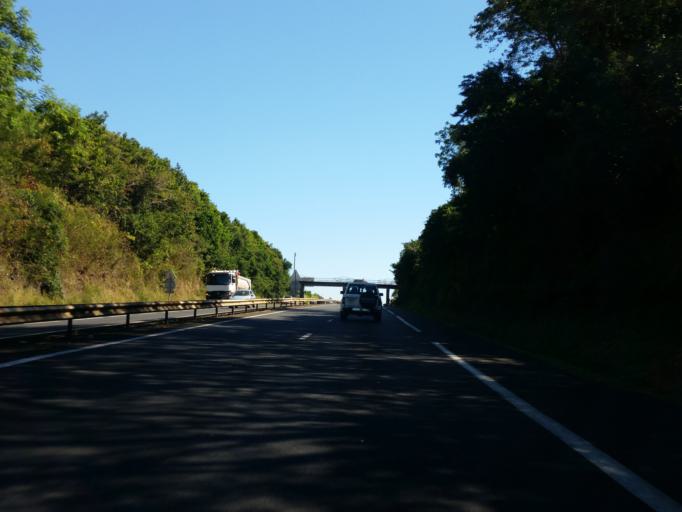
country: RE
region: Reunion
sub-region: Reunion
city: Sainte-Marie
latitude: -20.8980
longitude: 55.5720
